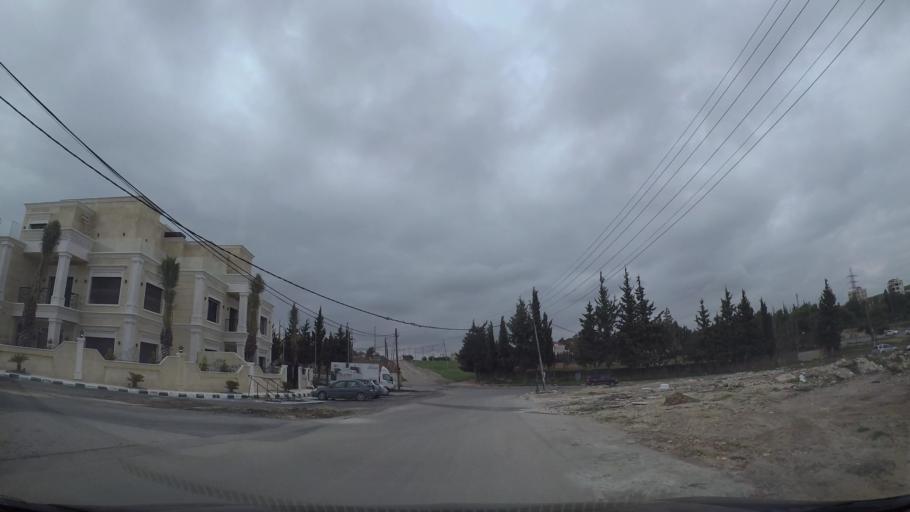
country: JO
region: Amman
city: Umm as Summaq
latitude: 31.9273
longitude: 35.8585
